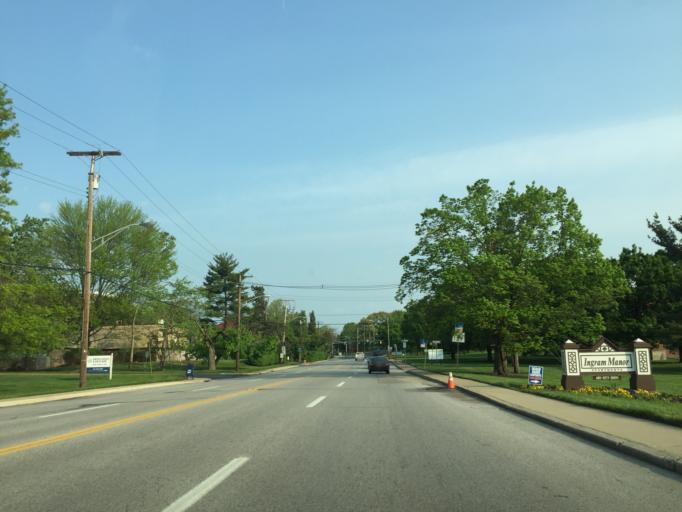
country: US
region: Maryland
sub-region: Baltimore County
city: Pikesville
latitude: 39.3703
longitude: -76.7093
